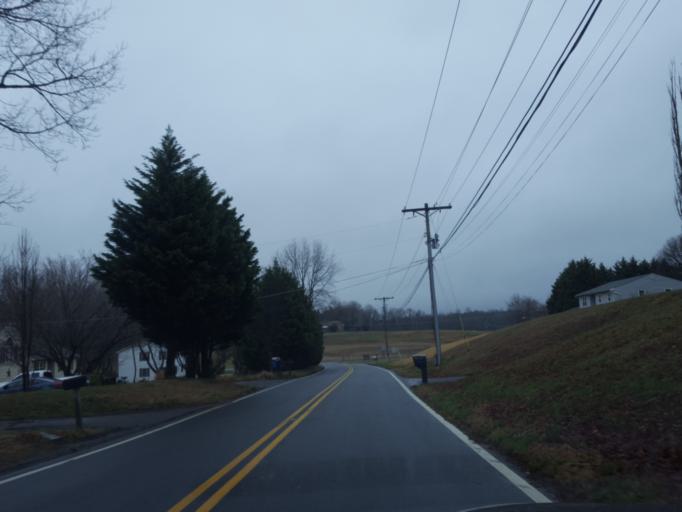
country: US
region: Maryland
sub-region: Calvert County
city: Huntingtown
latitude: 38.6143
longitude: -76.5486
